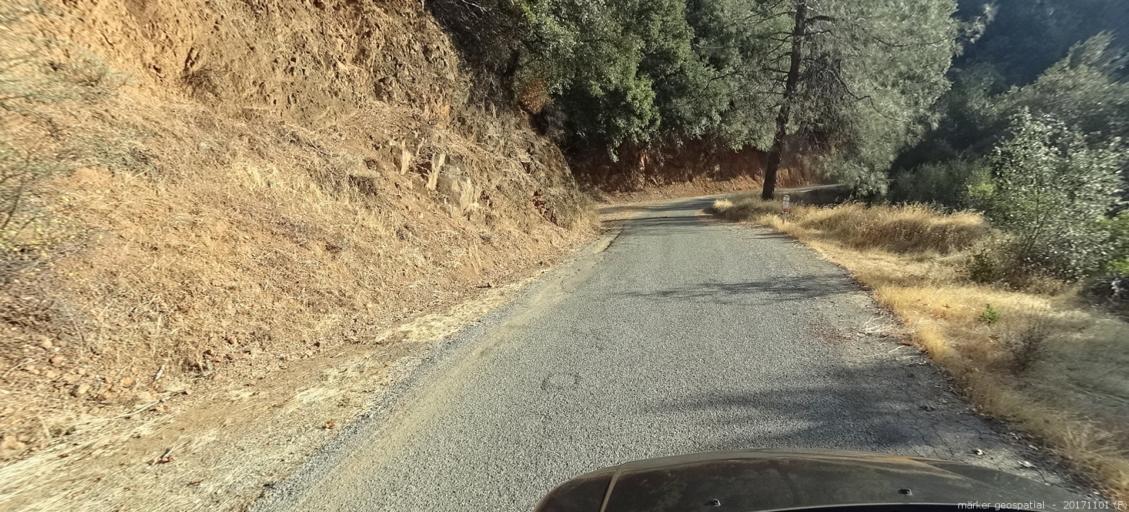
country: US
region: California
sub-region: Shasta County
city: Shasta Lake
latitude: 40.8103
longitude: -122.3157
